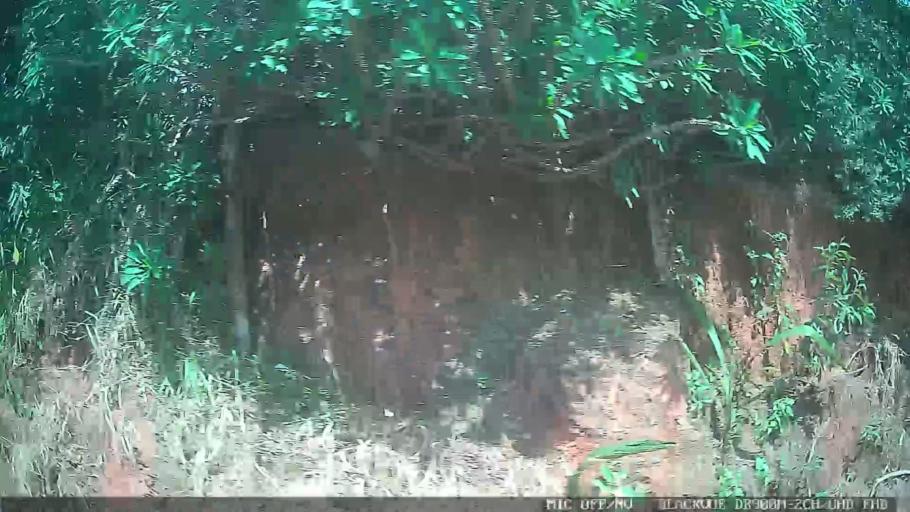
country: BR
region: Sao Paulo
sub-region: Atibaia
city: Atibaia
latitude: -23.0889
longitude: -46.5441
